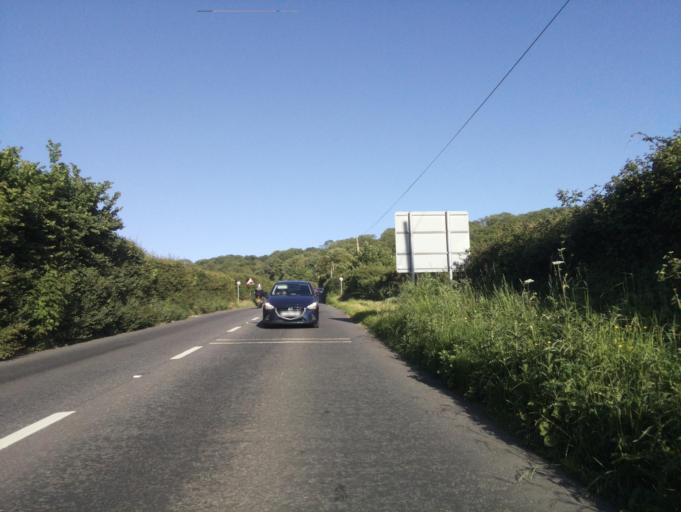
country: GB
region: England
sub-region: Devon
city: Sidmouth
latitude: 50.7012
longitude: -3.2176
